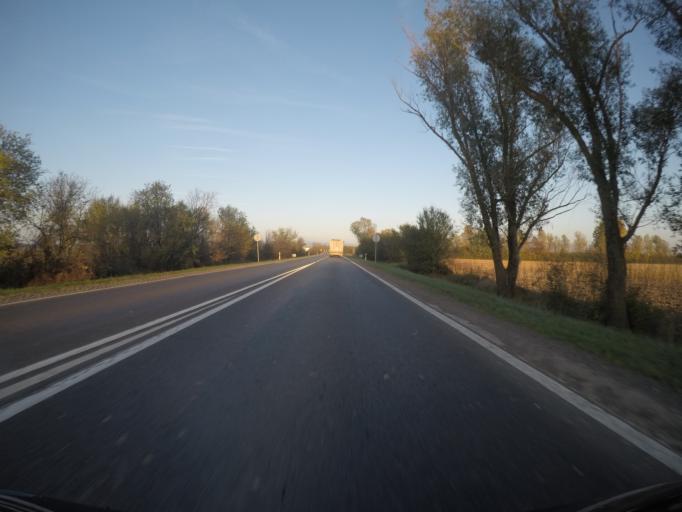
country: HU
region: Baranya
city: Szentlorinc
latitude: 46.0414
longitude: 17.9698
